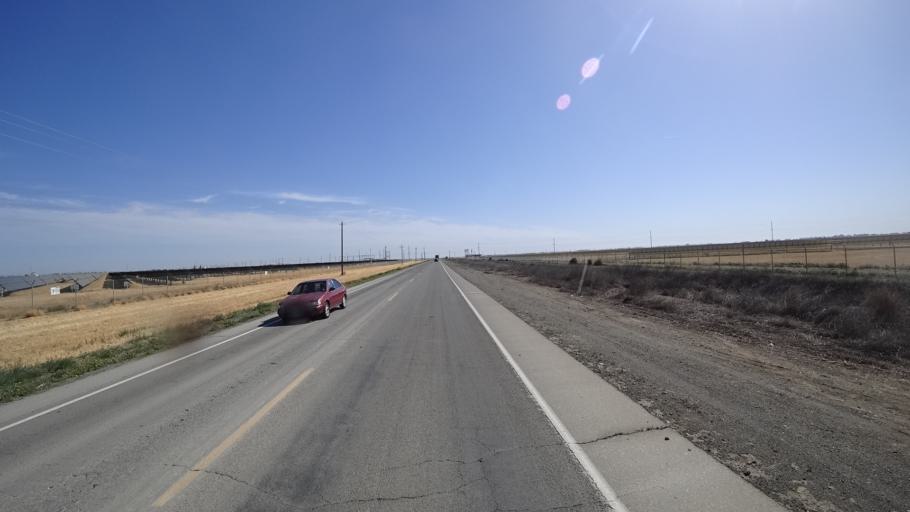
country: US
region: California
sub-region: Kings County
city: Lemoore Station
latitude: 36.2173
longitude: -119.9096
